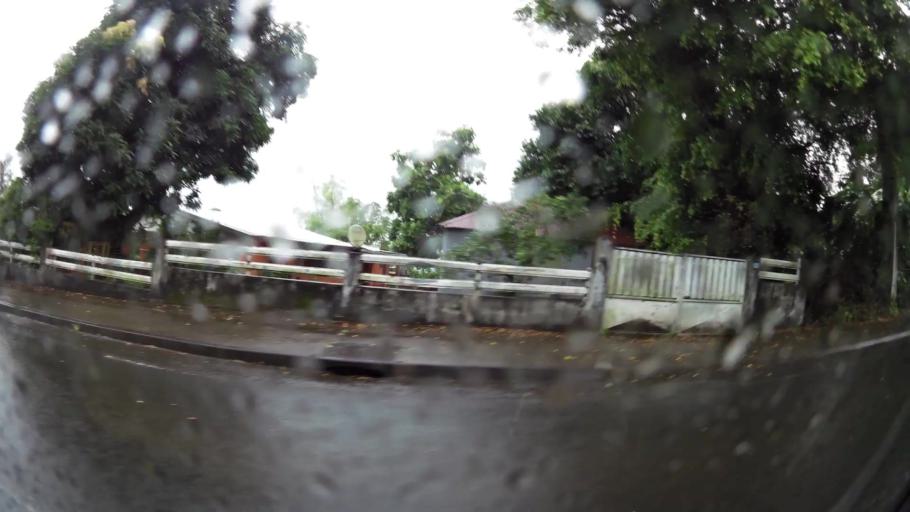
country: RE
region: Reunion
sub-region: Reunion
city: Saint-Benoit
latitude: -21.0223
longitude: 55.6988
